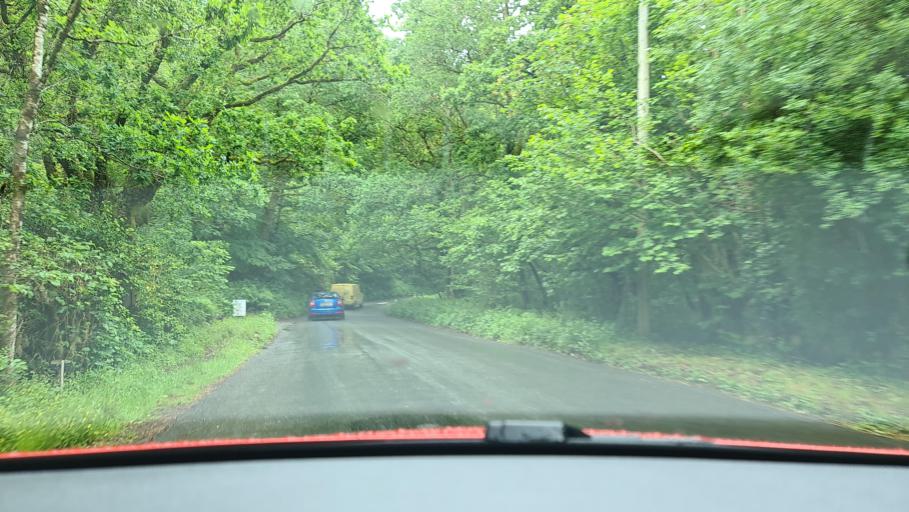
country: GB
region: England
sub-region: Cornwall
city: Liskeard
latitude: 50.4722
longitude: -4.5565
